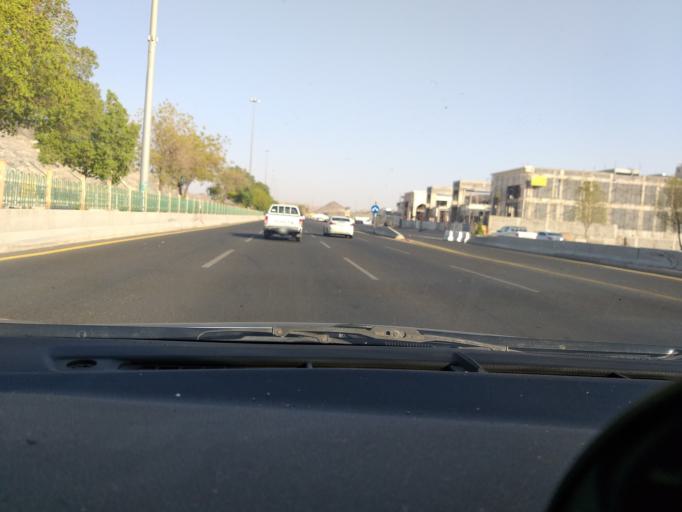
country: SA
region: Makkah
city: Mecca
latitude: 21.3720
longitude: 39.8820
